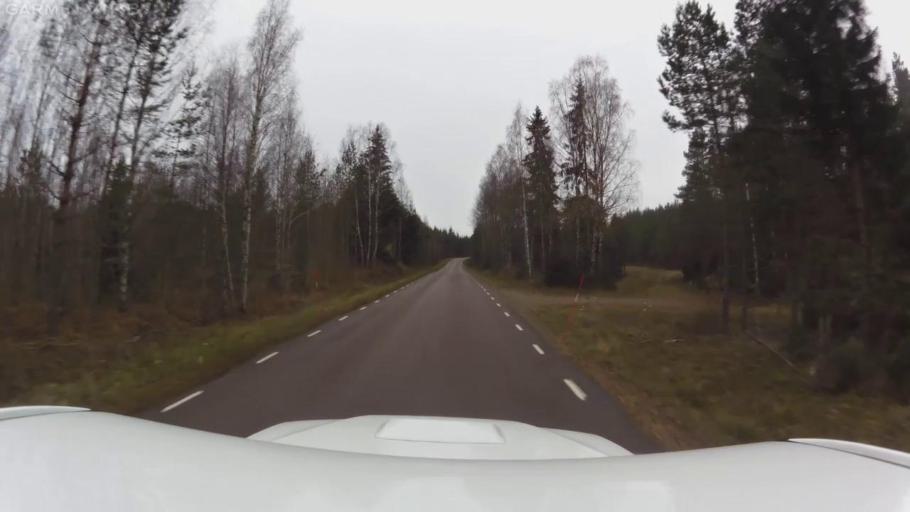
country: SE
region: OEstergoetland
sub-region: Mjolby Kommun
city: Mantorp
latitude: 58.1633
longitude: 15.3964
